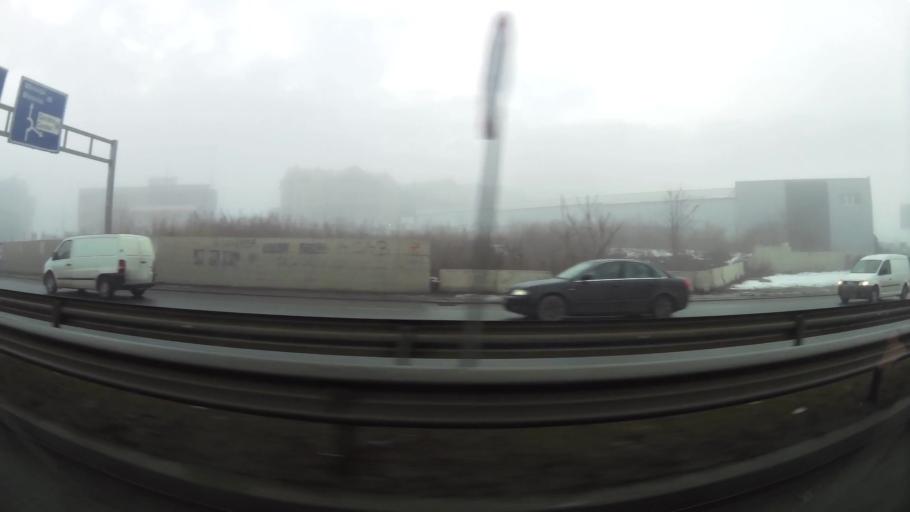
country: XK
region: Pristina
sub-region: Komuna e Prishtines
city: Pristina
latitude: 42.6572
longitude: 21.1378
